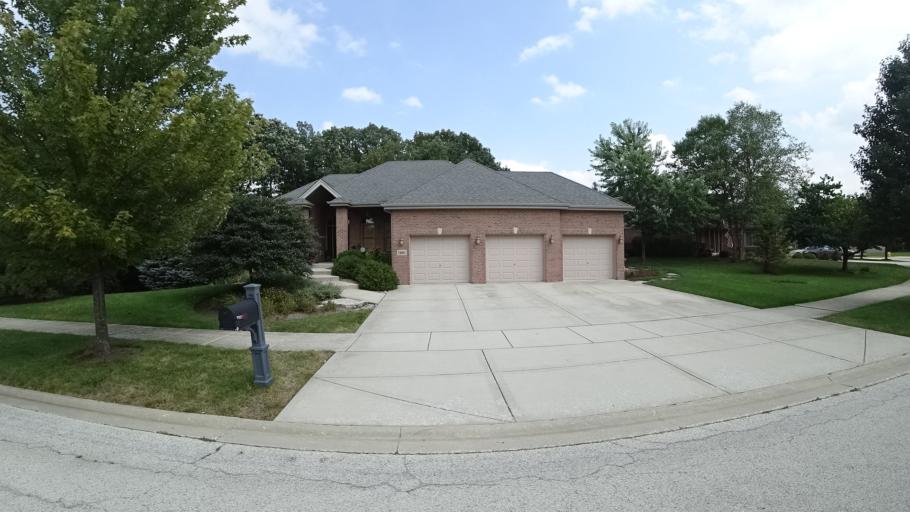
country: US
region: Illinois
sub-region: Will County
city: Goodings Grove
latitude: 41.6346
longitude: -87.9057
